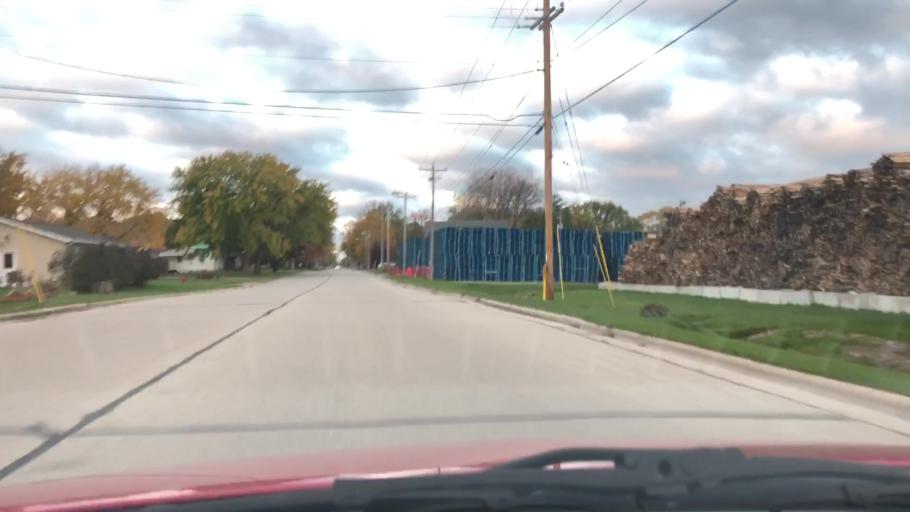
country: US
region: Wisconsin
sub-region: Outagamie County
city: Seymour
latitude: 44.5104
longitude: -88.3232
